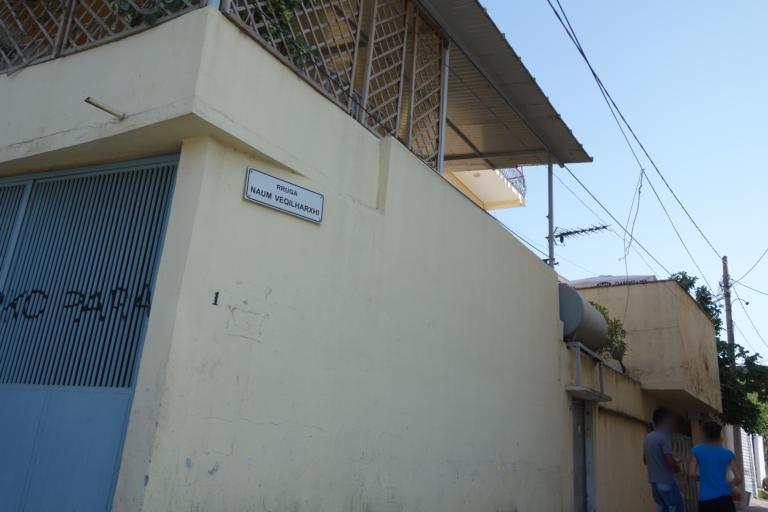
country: AL
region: Tirane
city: Tirana
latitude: 41.3364
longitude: 19.8436
